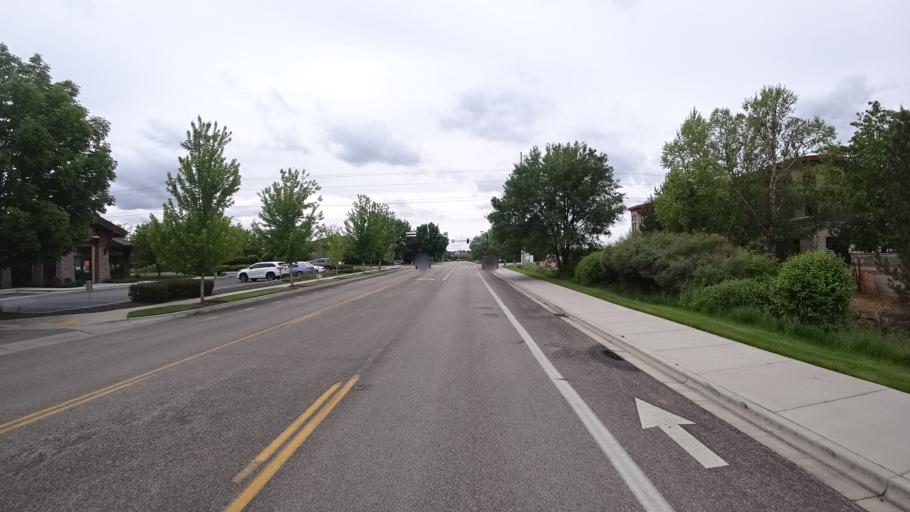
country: US
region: Idaho
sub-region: Ada County
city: Eagle
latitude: 43.6940
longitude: -116.3400
